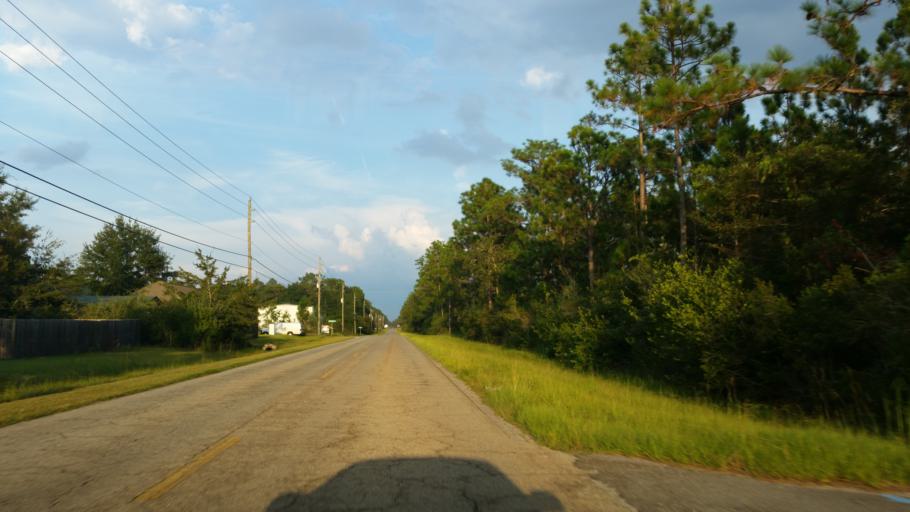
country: US
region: Florida
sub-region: Santa Rosa County
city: Bagdad
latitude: 30.5442
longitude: -87.0952
